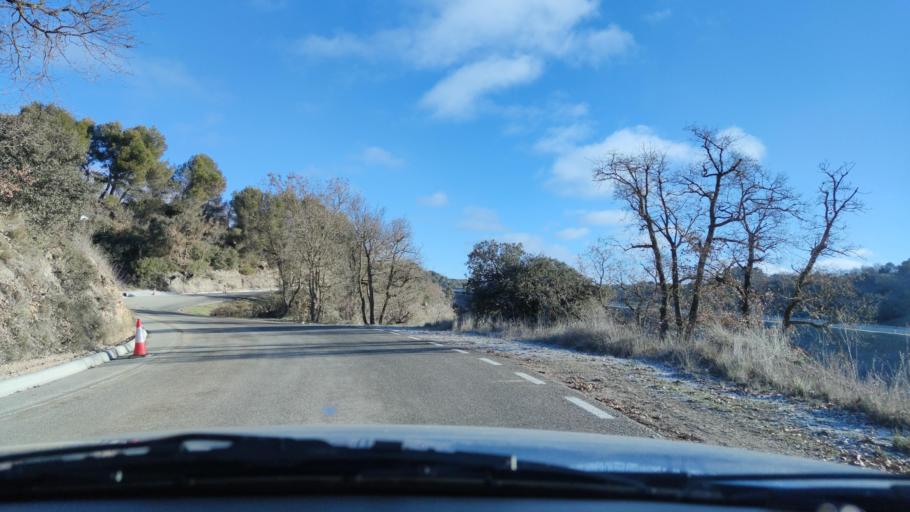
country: ES
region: Catalonia
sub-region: Provincia de Barcelona
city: Pujalt
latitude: 41.7006
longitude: 1.3483
